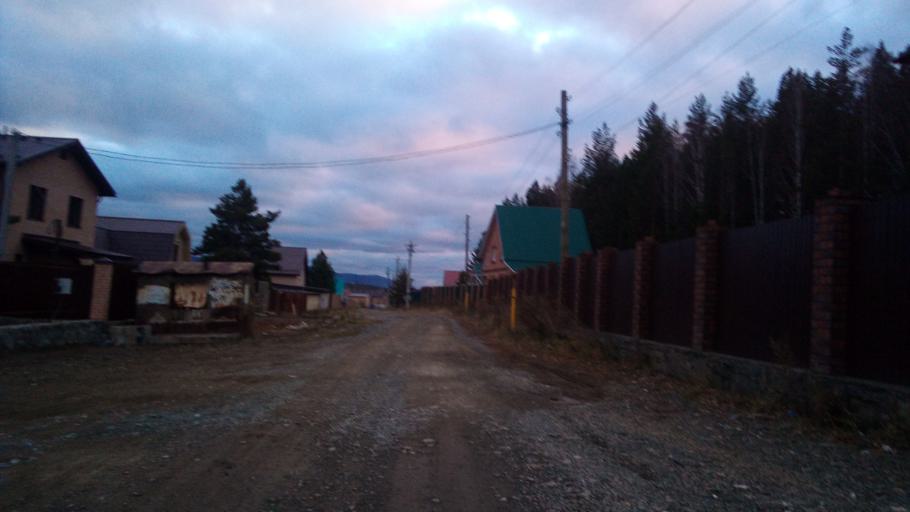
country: RU
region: Chelyabinsk
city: Turgoyak
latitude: 55.1770
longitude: 60.1312
